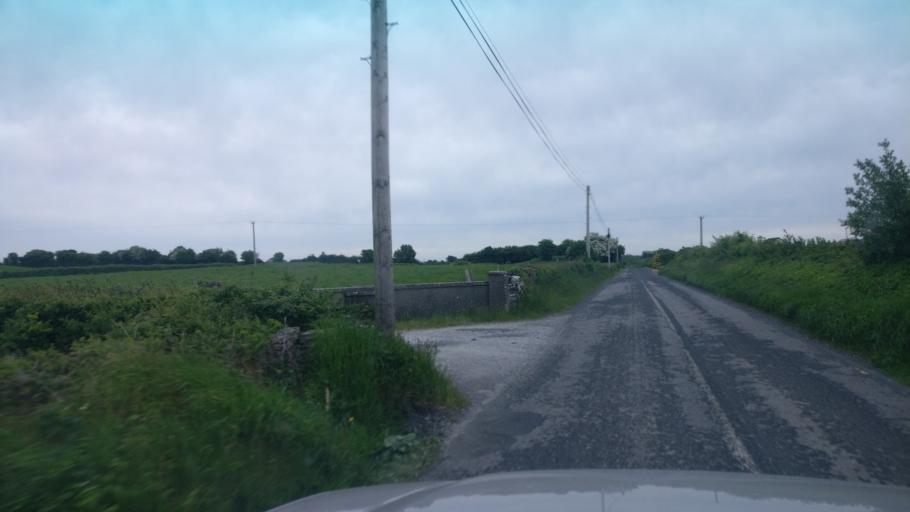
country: IE
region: Connaught
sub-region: County Galway
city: Portumna
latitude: 53.1116
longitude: -8.2751
